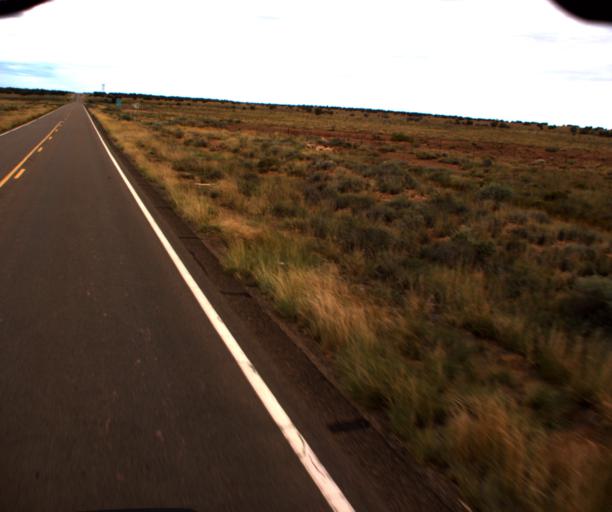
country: US
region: Arizona
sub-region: Navajo County
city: Snowflake
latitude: 34.6557
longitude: -110.0990
